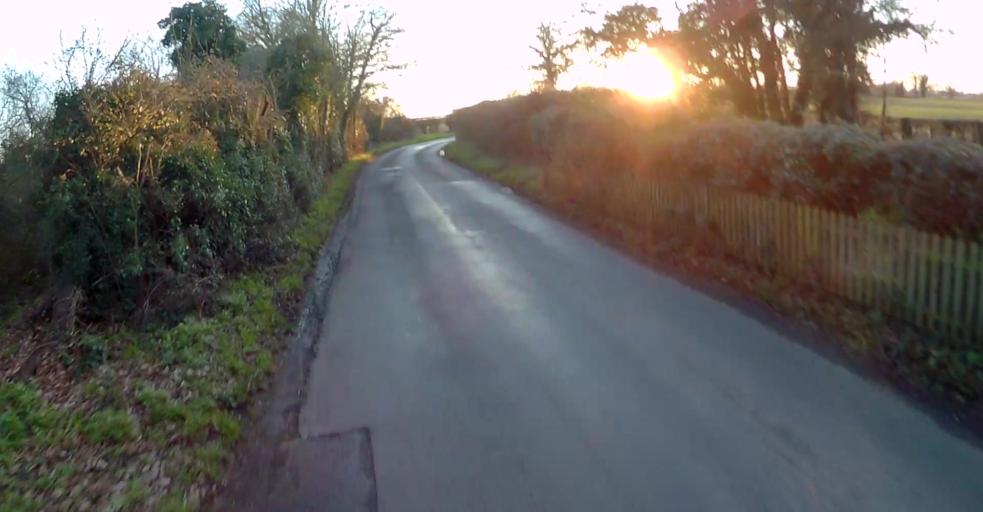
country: GB
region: England
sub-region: West Berkshire
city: Stratfield Mortimer
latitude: 51.3486
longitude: -1.0278
